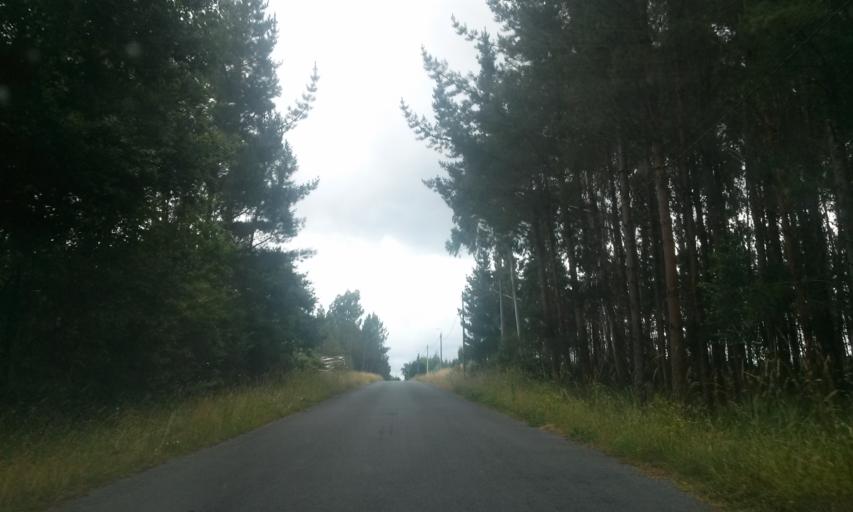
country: ES
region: Galicia
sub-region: Provincia de Lugo
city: Outeiro de Rei
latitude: 43.0769
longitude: -7.6297
